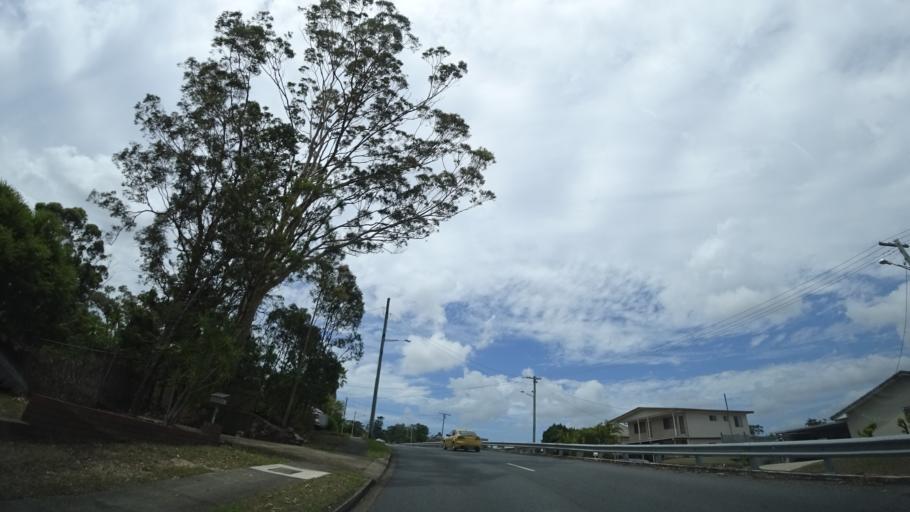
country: AU
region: Queensland
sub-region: Brisbane
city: Everton Park
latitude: -27.3944
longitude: 152.9671
